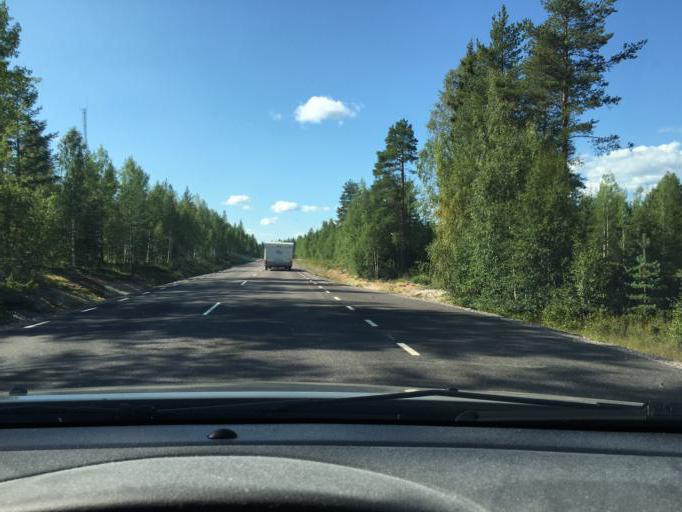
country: SE
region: Norrbotten
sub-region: Lulea Kommun
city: Ranea
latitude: 66.0505
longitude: 22.2269
